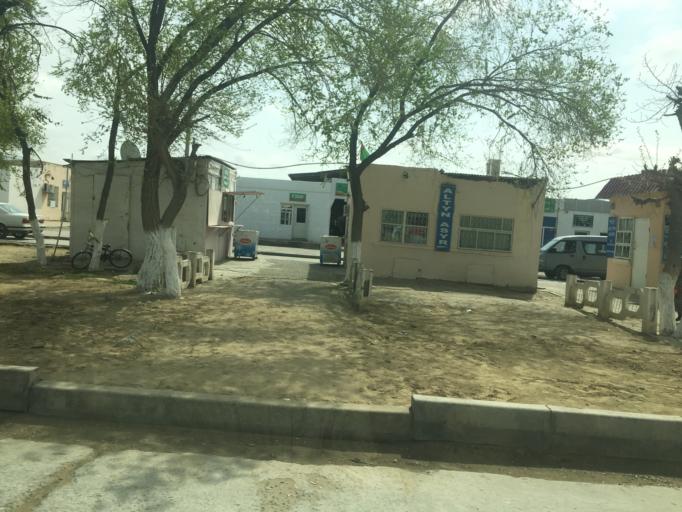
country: TM
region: Mary
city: Seydi
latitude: 39.4812
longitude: 62.9114
